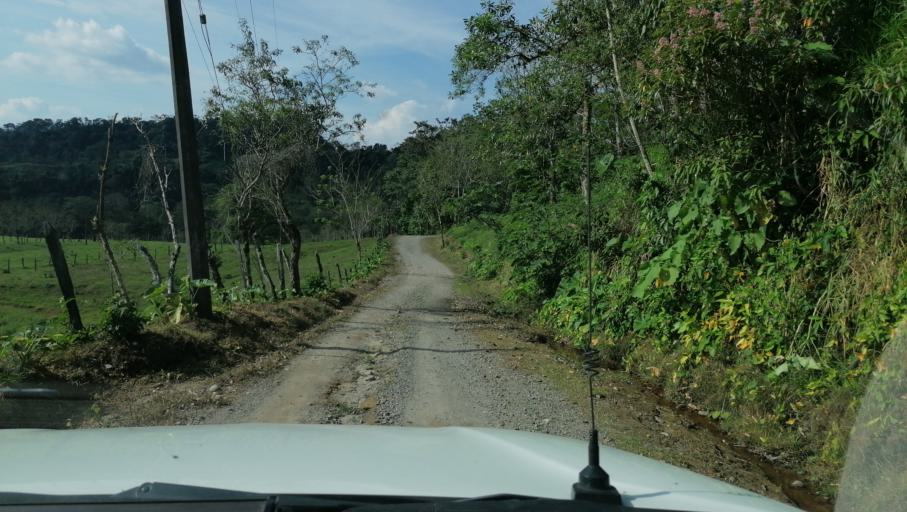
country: MX
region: Chiapas
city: Ostuacan
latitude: 17.4702
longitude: -93.2359
